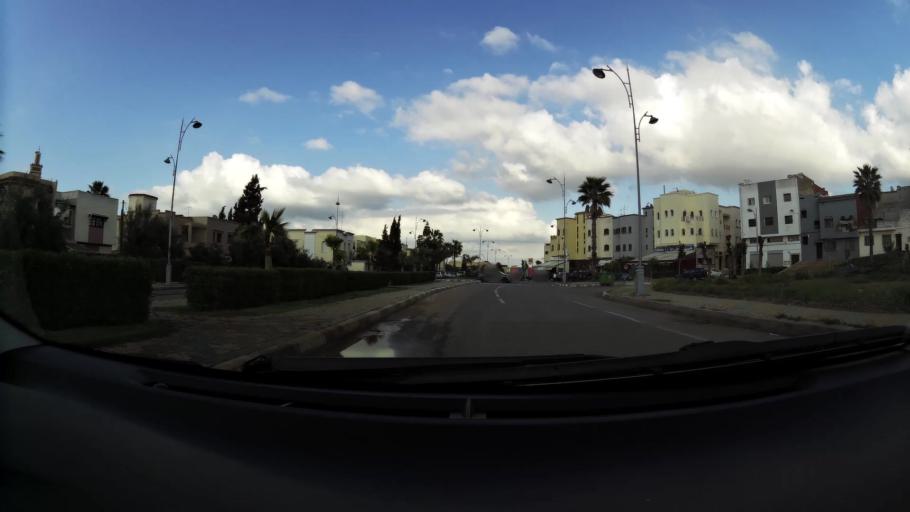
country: MA
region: Chaouia-Ouardigha
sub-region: Settat Province
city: Settat
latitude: 33.0084
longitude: -7.6318
